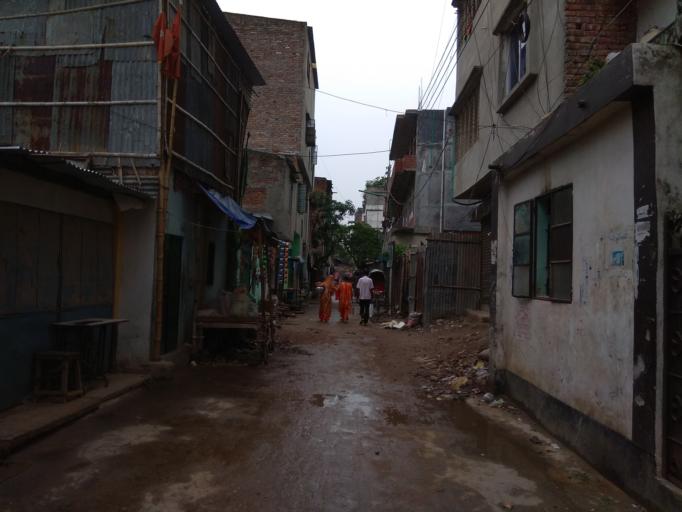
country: BD
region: Dhaka
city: Tungi
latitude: 23.8233
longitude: 90.3733
